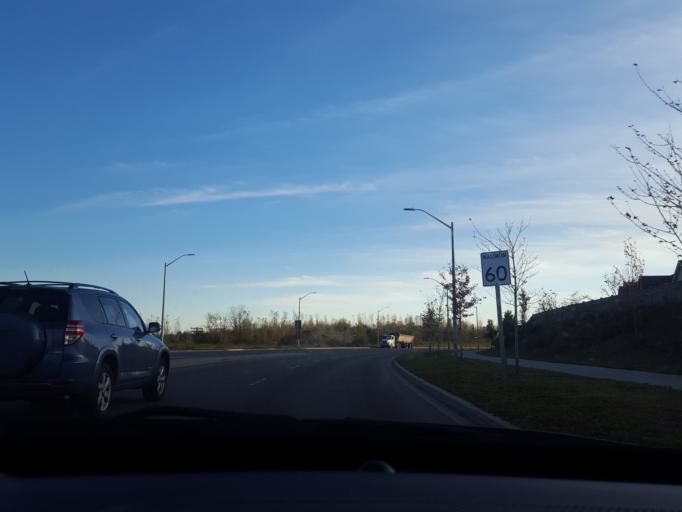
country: CA
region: Ontario
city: Markham
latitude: 43.8688
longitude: -79.2116
